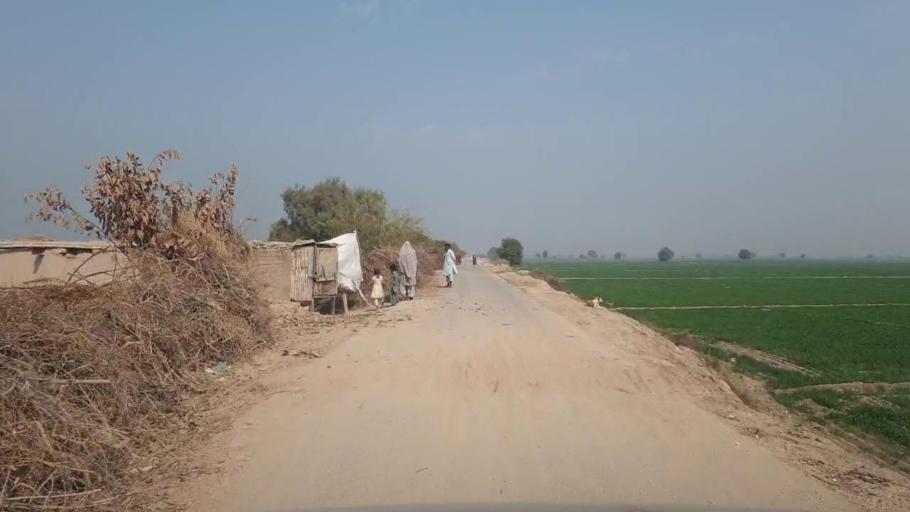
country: PK
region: Sindh
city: Hala
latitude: 25.7740
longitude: 68.3939
